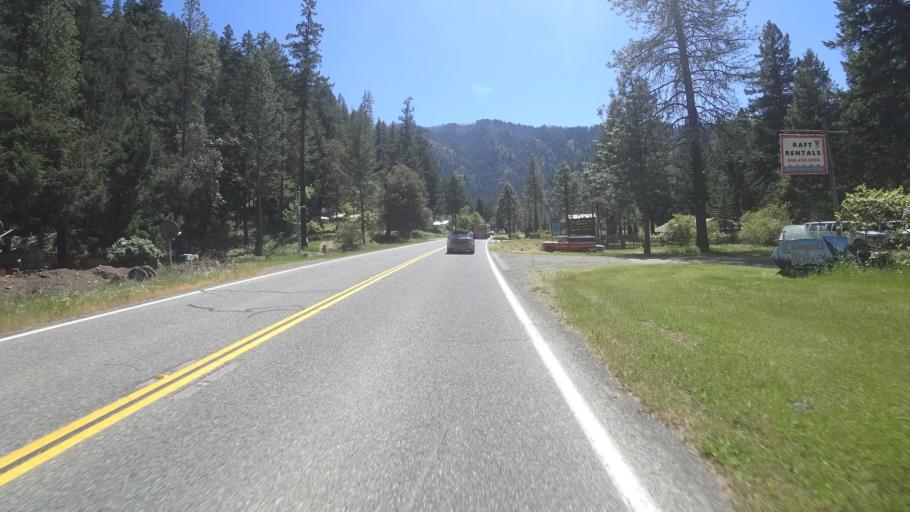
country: US
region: California
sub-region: Trinity County
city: Hayfork
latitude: 40.7790
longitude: -123.3321
